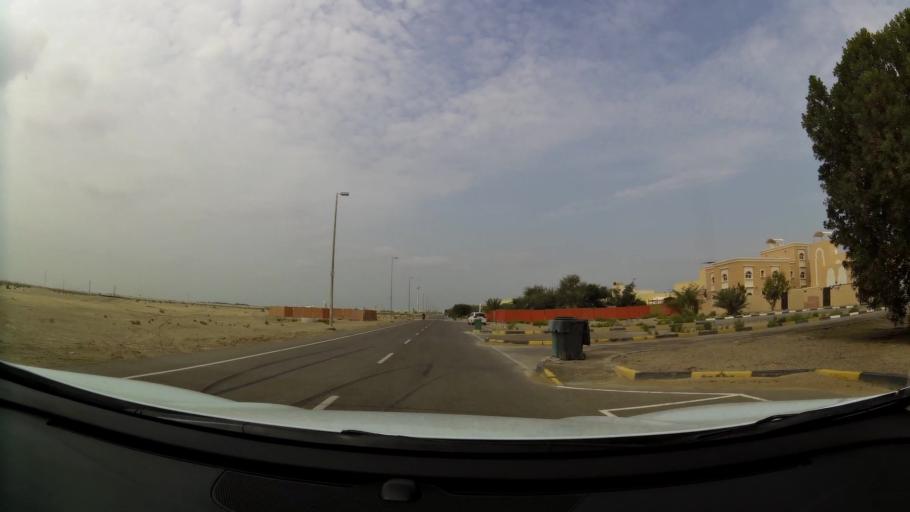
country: AE
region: Abu Dhabi
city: Abu Dhabi
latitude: 24.6329
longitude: 54.6755
